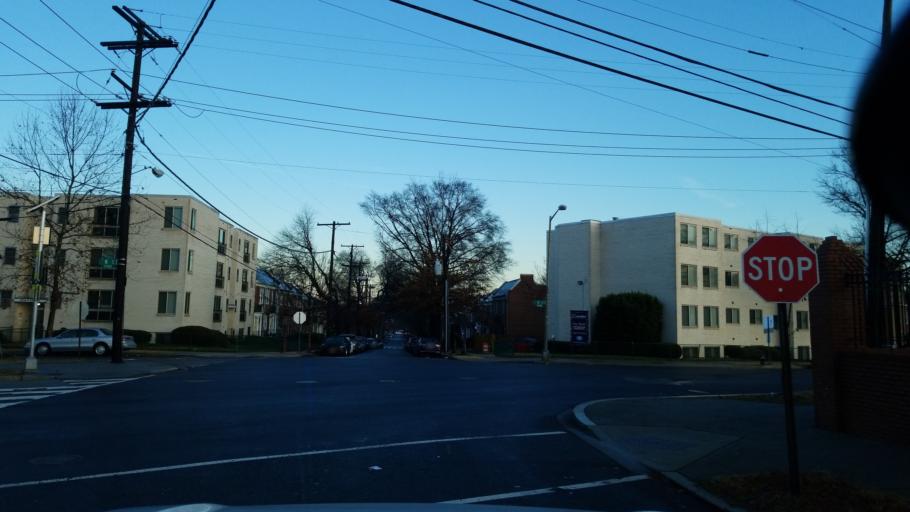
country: US
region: Maryland
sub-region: Prince George's County
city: Hillcrest Heights
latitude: 38.8692
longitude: -76.9790
